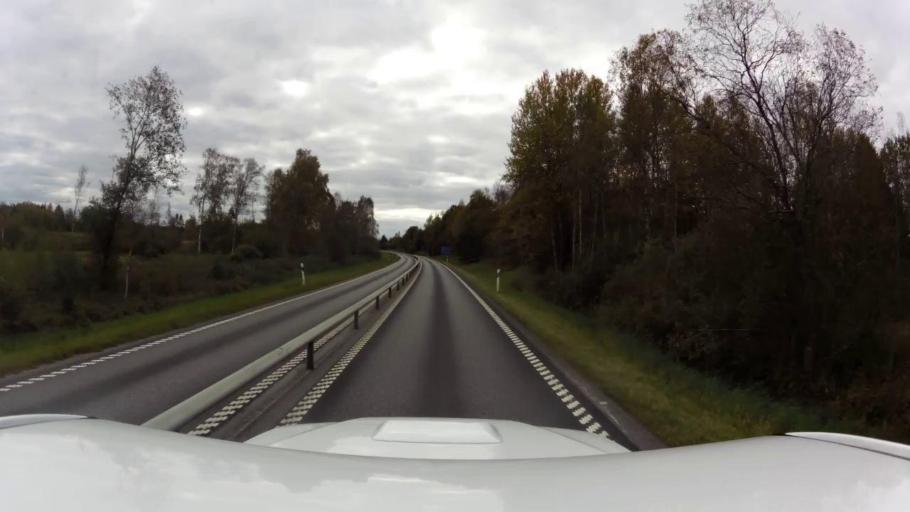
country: SE
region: OEstergoetland
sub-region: Linkopings Kommun
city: Malmslatt
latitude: 58.2926
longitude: 15.5648
